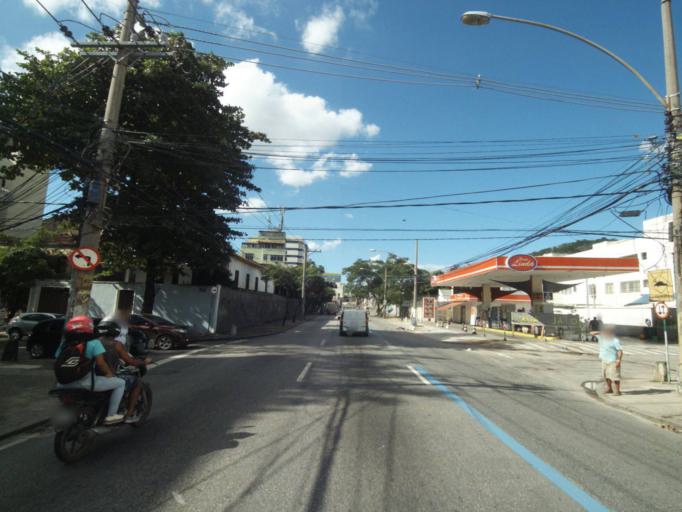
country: BR
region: Rio de Janeiro
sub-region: Rio De Janeiro
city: Rio de Janeiro
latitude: -22.9034
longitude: -43.2553
